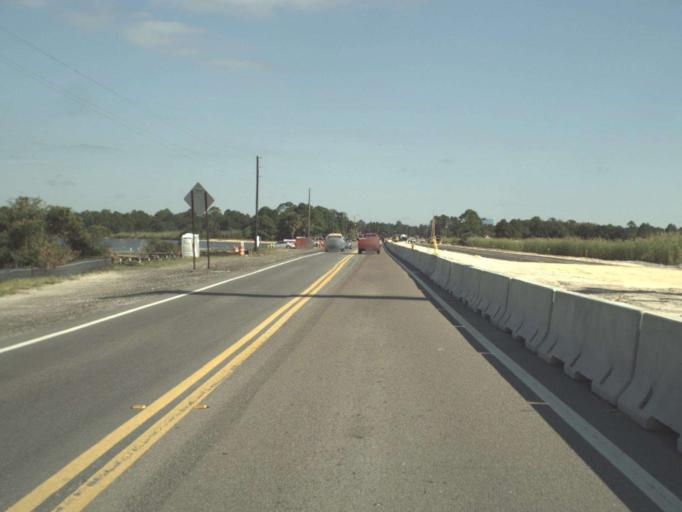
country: US
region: Florida
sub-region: Walton County
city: Freeport
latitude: 30.4274
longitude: -86.1559
